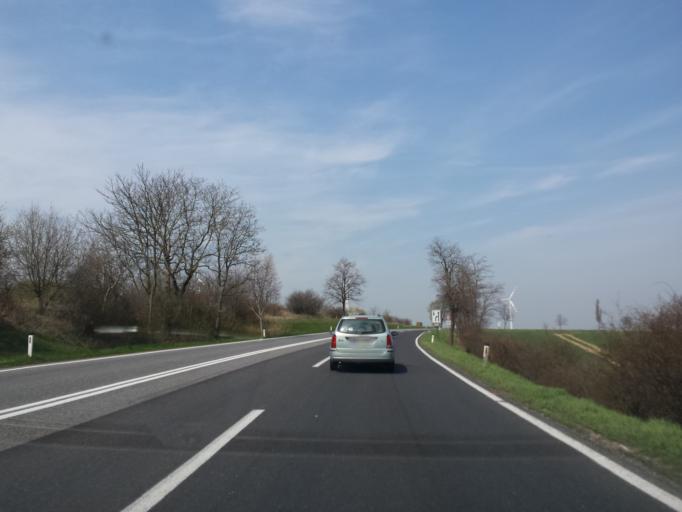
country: AT
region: Lower Austria
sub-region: Politischer Bezirk Mistelbach
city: Wilfersdorf
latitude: 48.5941
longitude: 16.6469
